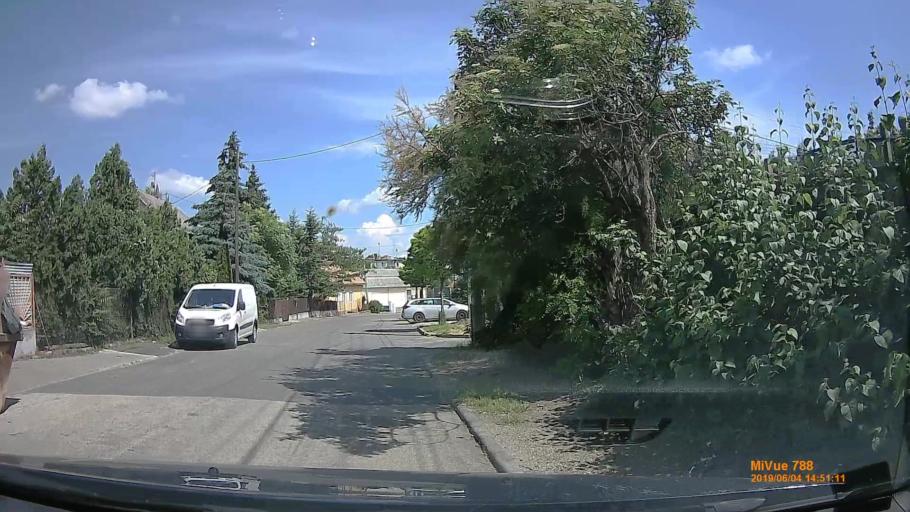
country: HU
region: Budapest
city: Budapest XXII. keruelet
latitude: 47.4193
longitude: 19.0355
